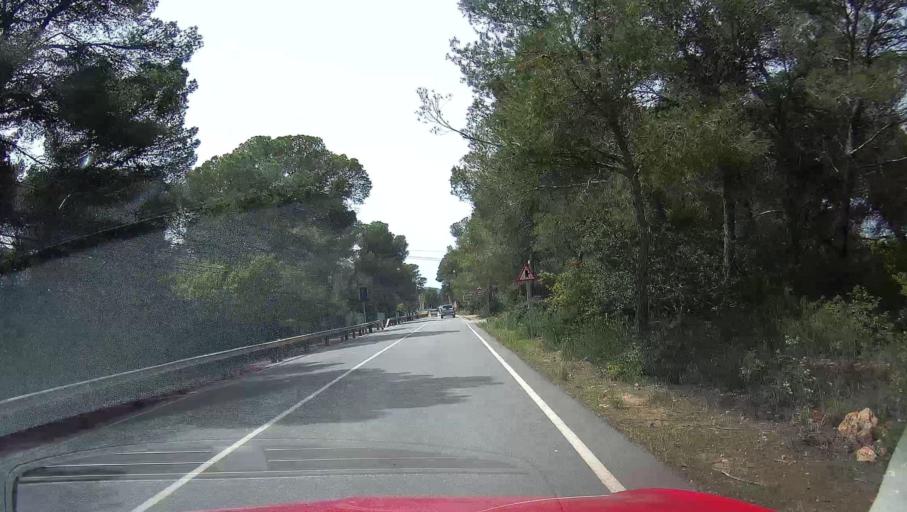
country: ES
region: Balearic Islands
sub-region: Illes Balears
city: Santa Eularia des Riu
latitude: 38.9997
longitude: 1.5617
